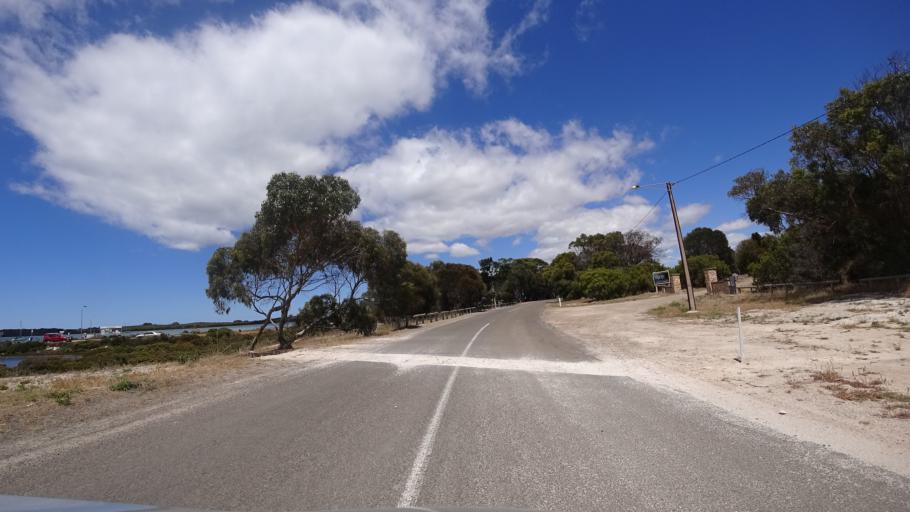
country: AU
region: South Australia
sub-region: Kangaroo Island
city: Kingscote
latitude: -35.7867
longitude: 137.7723
